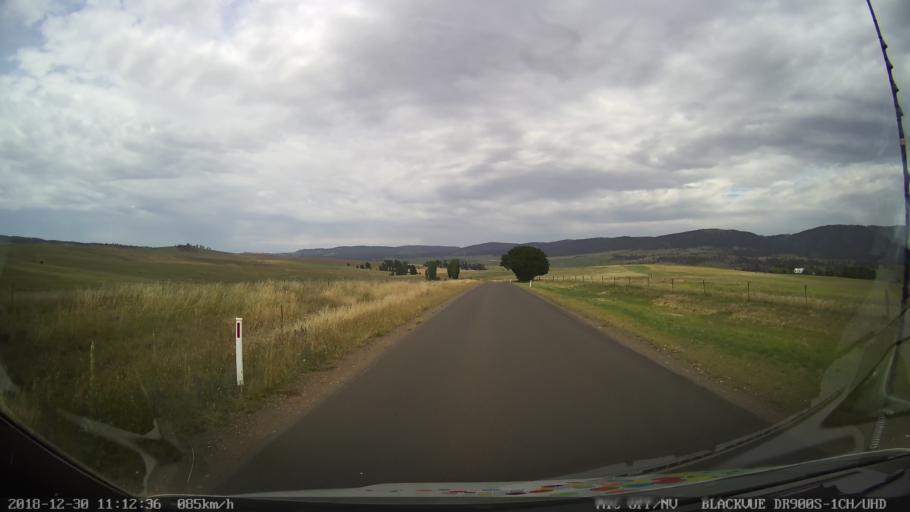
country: AU
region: New South Wales
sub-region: Snowy River
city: Jindabyne
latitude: -36.5294
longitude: 148.7544
